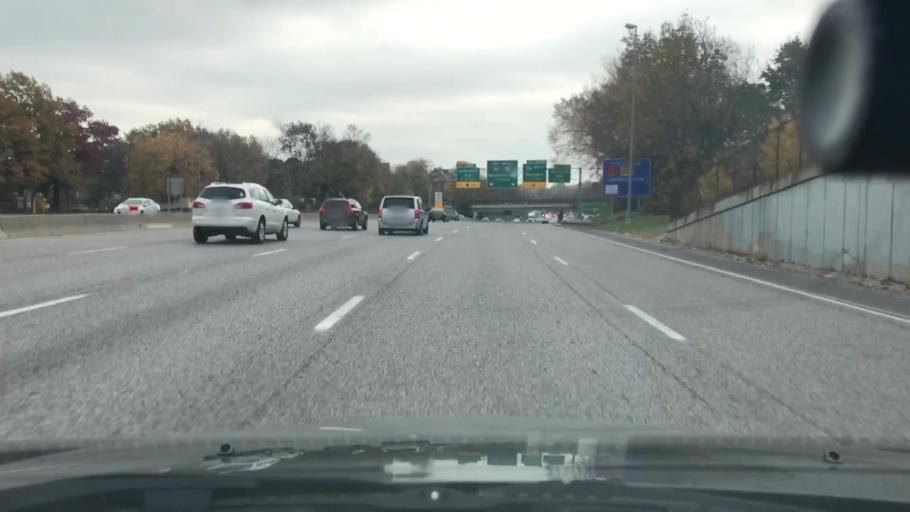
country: US
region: Missouri
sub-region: City of Saint Louis
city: St. Louis
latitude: 38.6162
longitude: -90.2362
